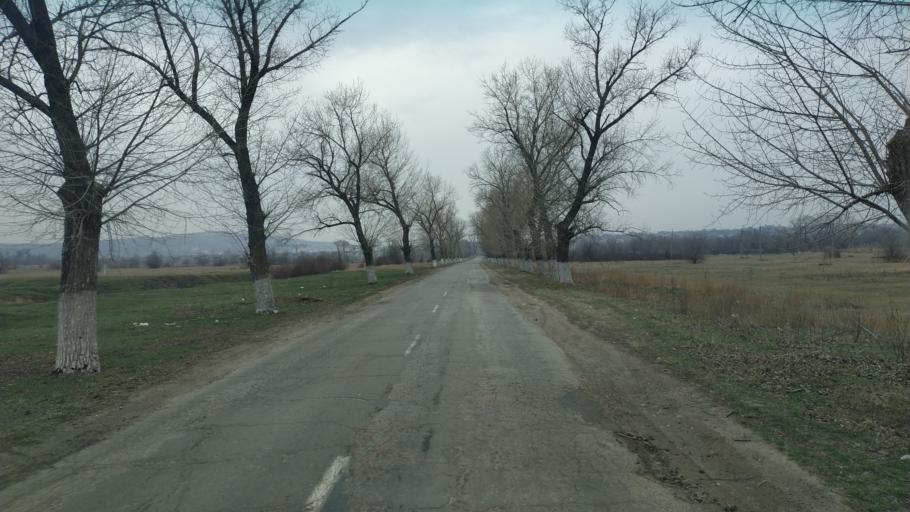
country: MD
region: Chisinau
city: Singera
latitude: 46.9276
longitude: 28.9815
